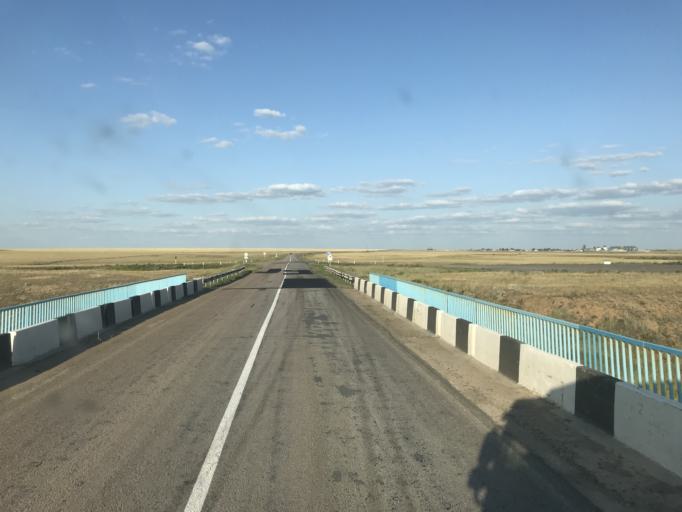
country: KZ
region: Aqmola
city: Atbasar
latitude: 51.8308
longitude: 67.8623
